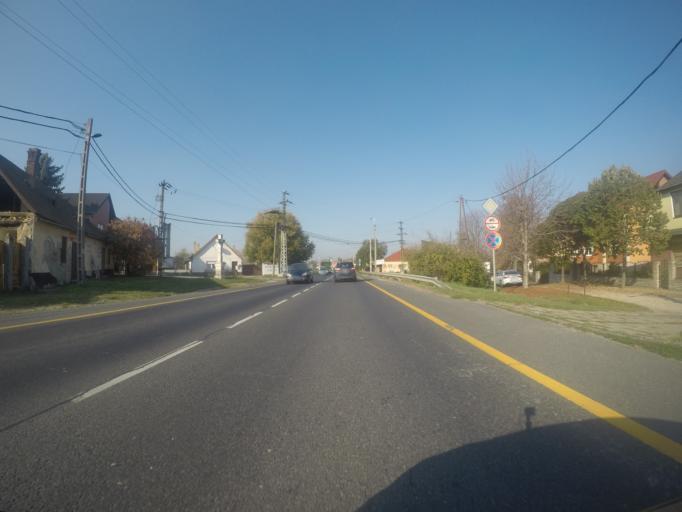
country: HU
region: Tolna
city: Dunafoldvar
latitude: 46.7999
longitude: 18.9180
